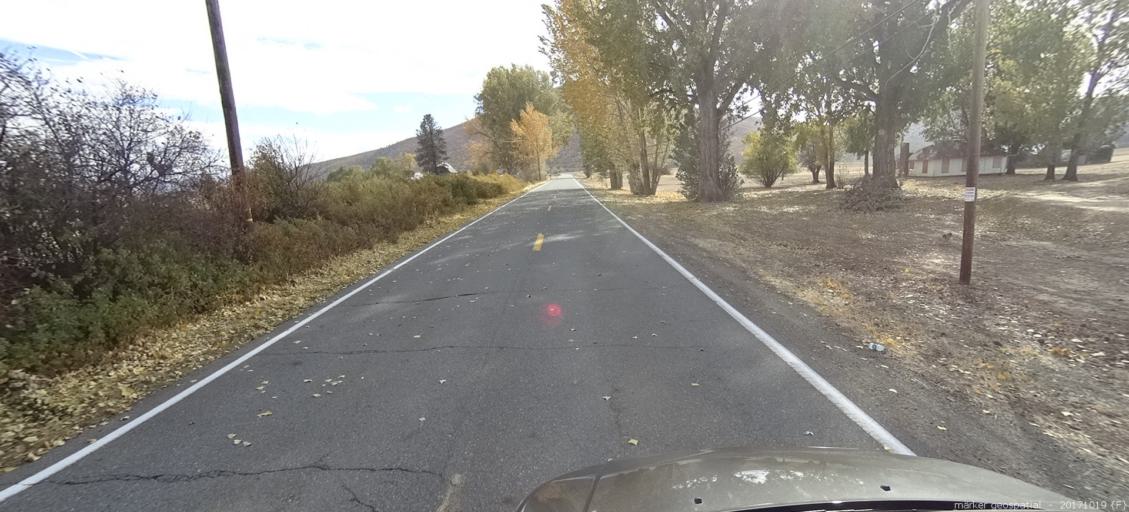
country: US
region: California
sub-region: Shasta County
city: Burney
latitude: 41.0489
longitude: -121.4947
